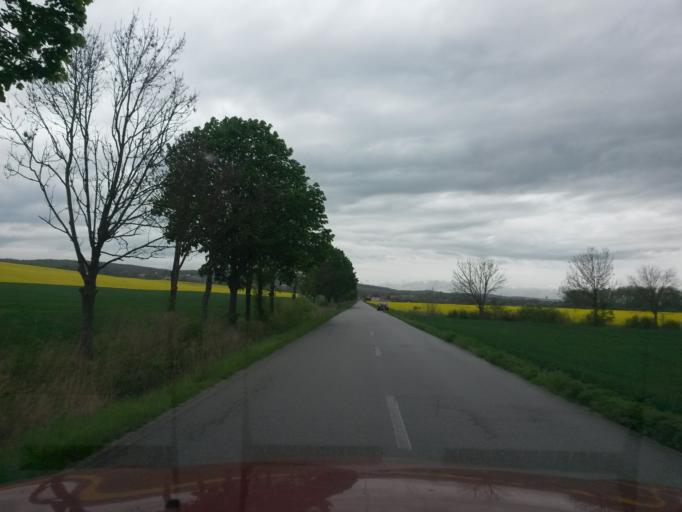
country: HU
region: Borsod-Abauj-Zemplen
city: Gonc
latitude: 48.5401
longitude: 21.2040
